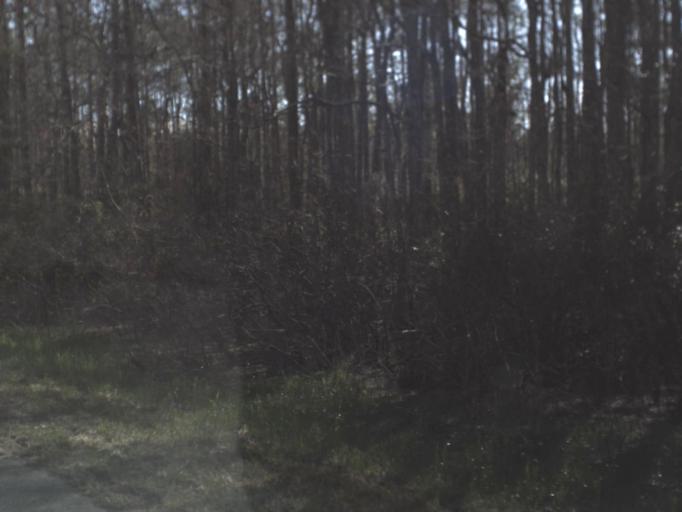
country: US
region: Florida
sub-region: Leon County
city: Woodville
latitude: 30.3440
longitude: -84.0064
